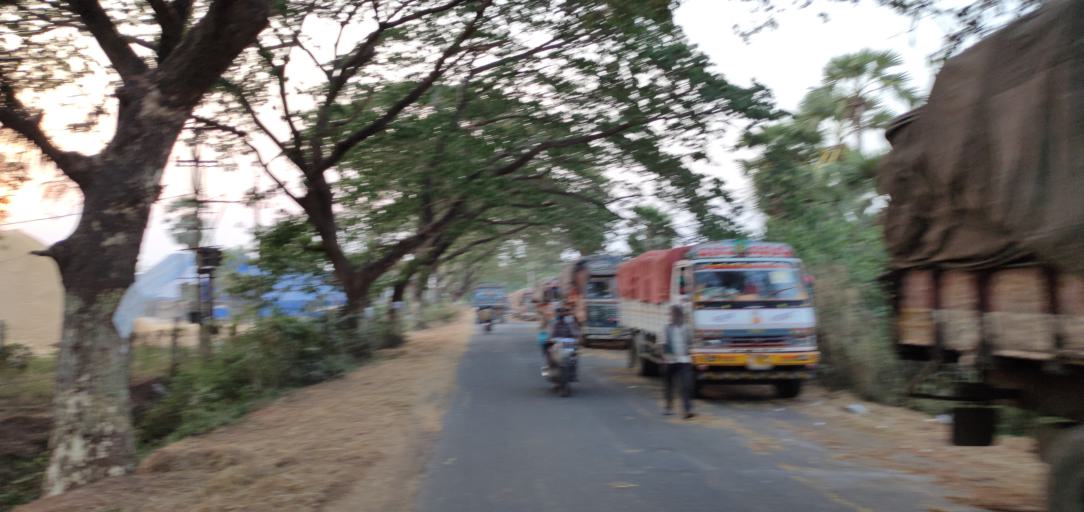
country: IN
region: Andhra Pradesh
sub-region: West Godavari
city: Tadepallegudem
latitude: 16.8472
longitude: 81.4906
